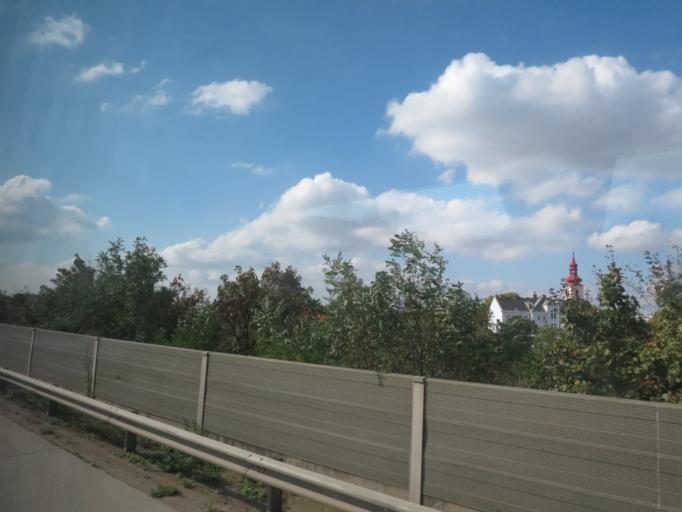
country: AT
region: Lower Austria
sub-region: Politischer Bezirk Wien-Umgebung
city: Schwechat
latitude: 48.1593
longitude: 16.4775
